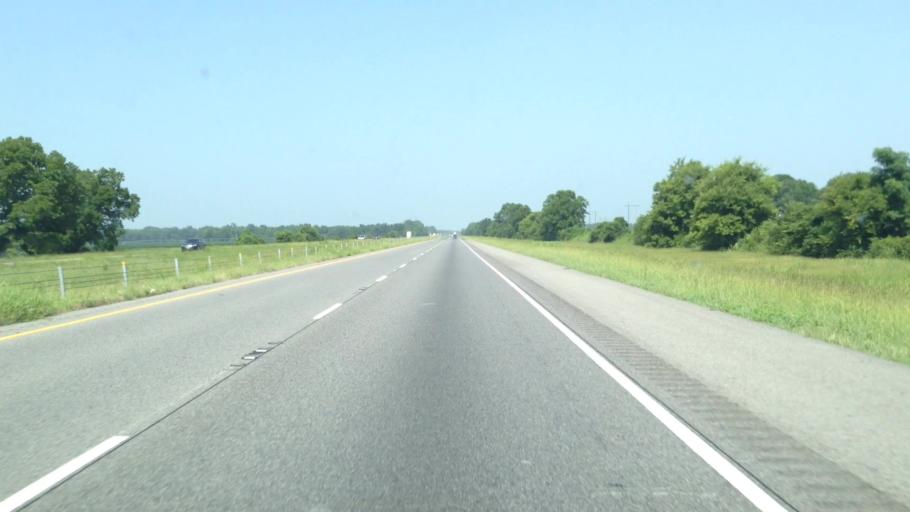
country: US
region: Louisiana
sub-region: Madison Parish
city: Tallulah
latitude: 32.4225
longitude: -91.3399
